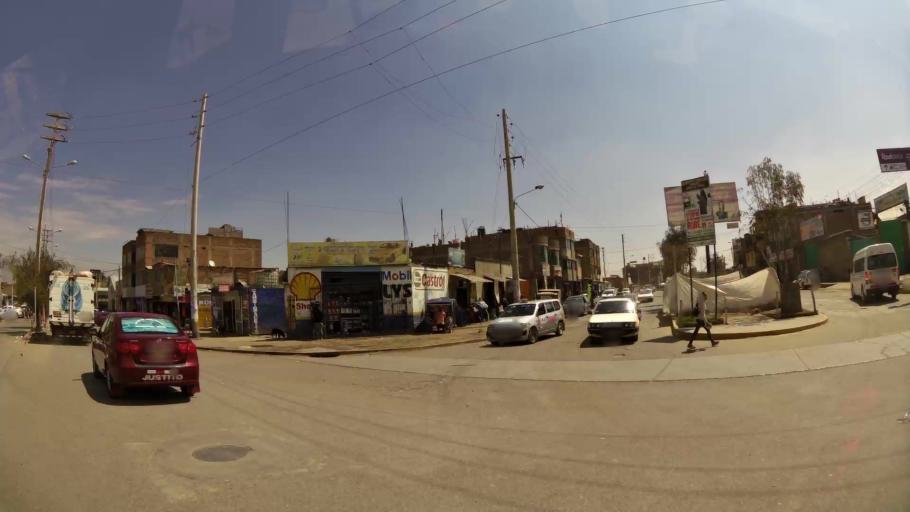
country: PE
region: Junin
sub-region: Provincia de Huancayo
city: Huancayo
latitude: -12.0775
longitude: -75.2003
